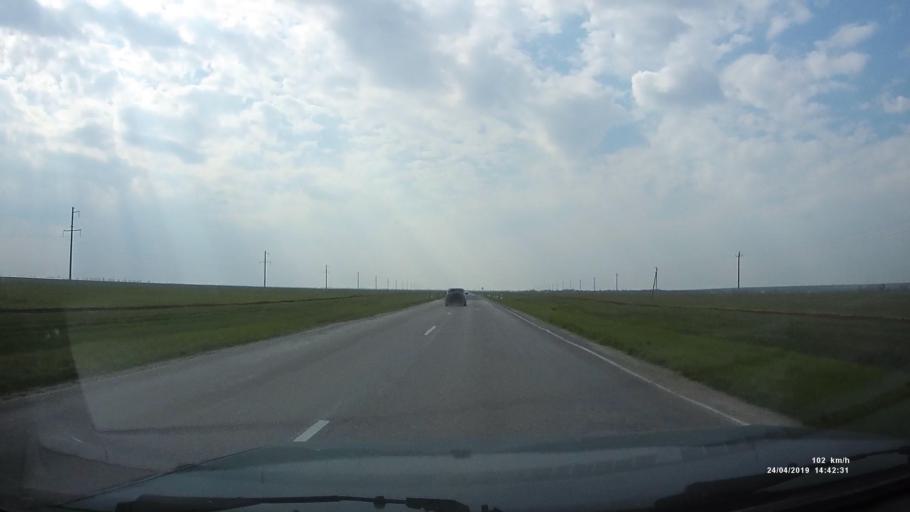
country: RU
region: Rostov
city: Remontnoye
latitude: 46.4523
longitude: 43.8604
